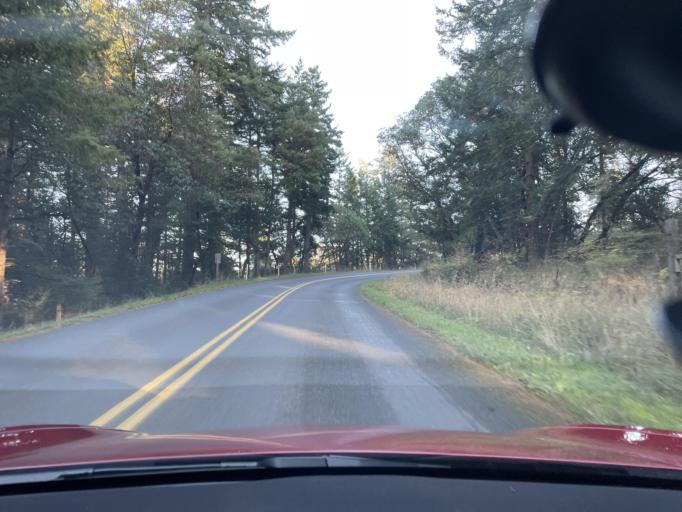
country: US
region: Washington
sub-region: San Juan County
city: Friday Harbor
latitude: 48.5652
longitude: -123.1552
